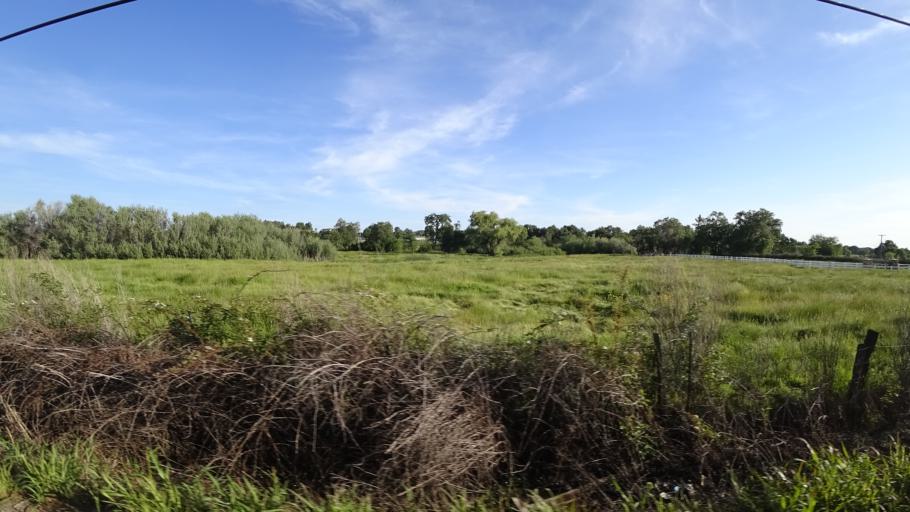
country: US
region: California
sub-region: Placer County
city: Lincoln
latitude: 38.9266
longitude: -121.2368
